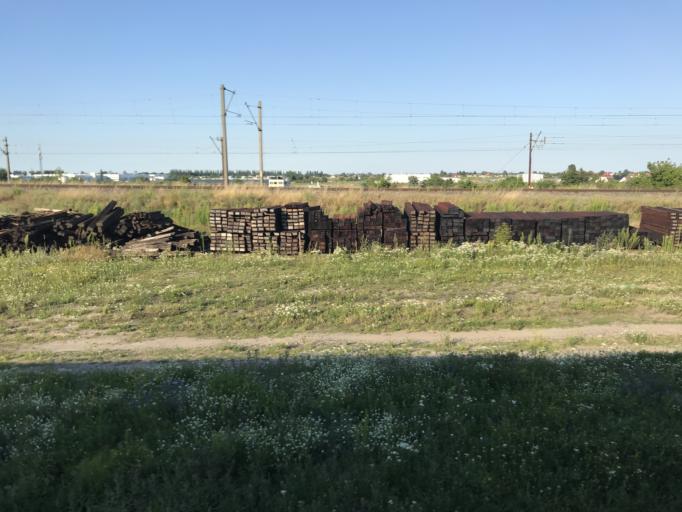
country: PL
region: Pomeranian Voivodeship
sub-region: Powiat tczewski
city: Tczew
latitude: 54.1033
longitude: 18.7844
